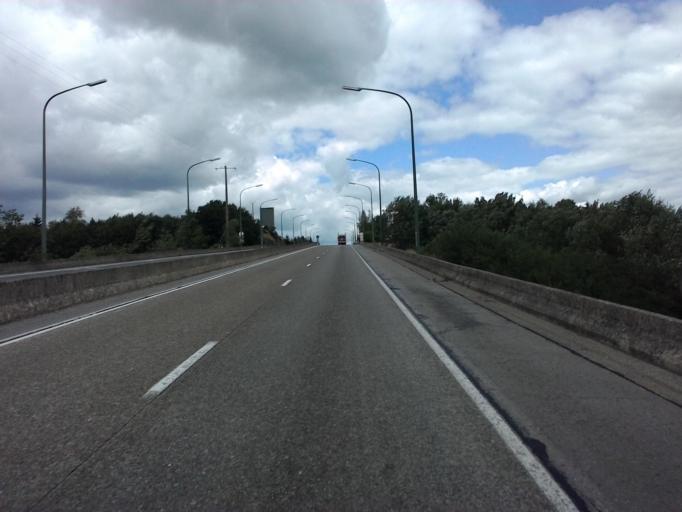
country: BE
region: Wallonia
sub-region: Province du Luxembourg
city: Martelange
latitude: 49.8446
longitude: 5.7328
